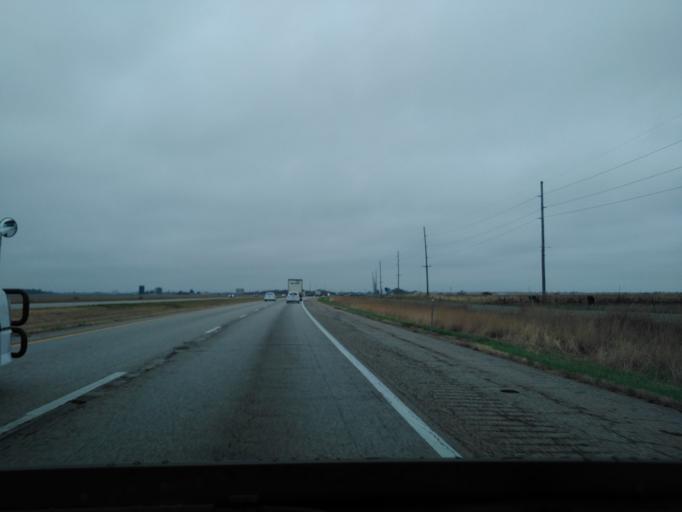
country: US
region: Illinois
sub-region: Madison County
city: Highland
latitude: 38.8172
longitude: -89.5646
